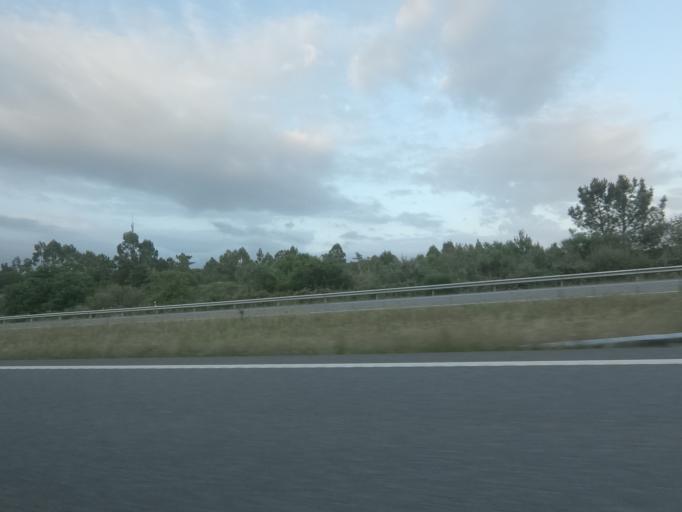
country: ES
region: Galicia
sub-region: Provincia de Ourense
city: Melon
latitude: 42.2305
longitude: -8.2343
